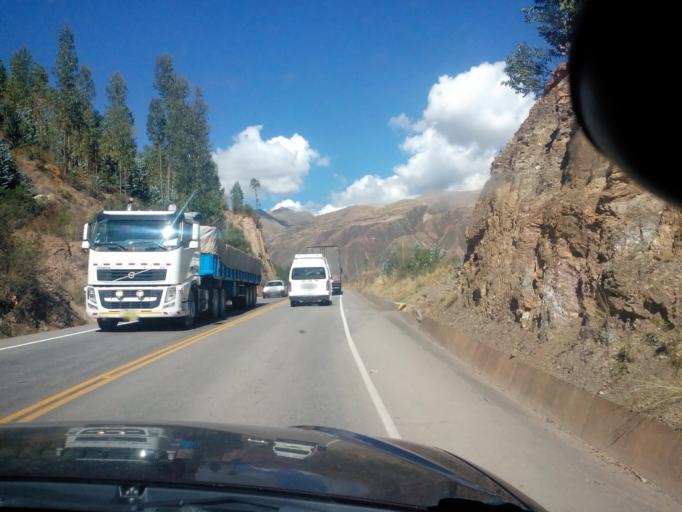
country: PE
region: Cusco
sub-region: Provincia de Quispicanchis
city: Urcos
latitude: -13.6901
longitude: -71.5951
